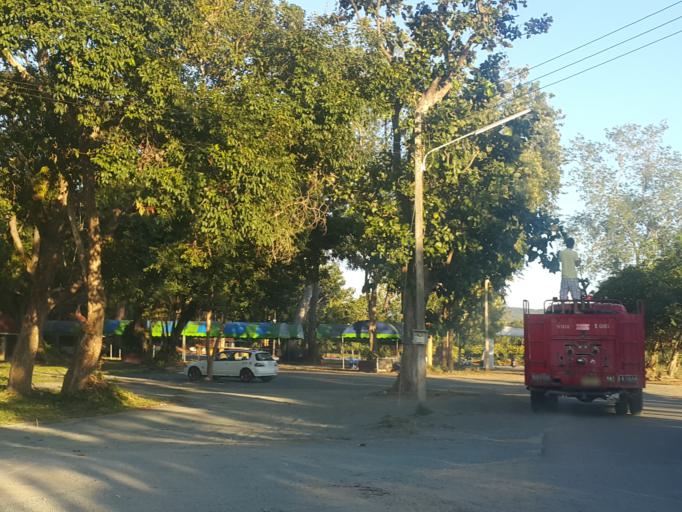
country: TH
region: Chiang Mai
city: San Sai
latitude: 18.8730
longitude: 99.1521
